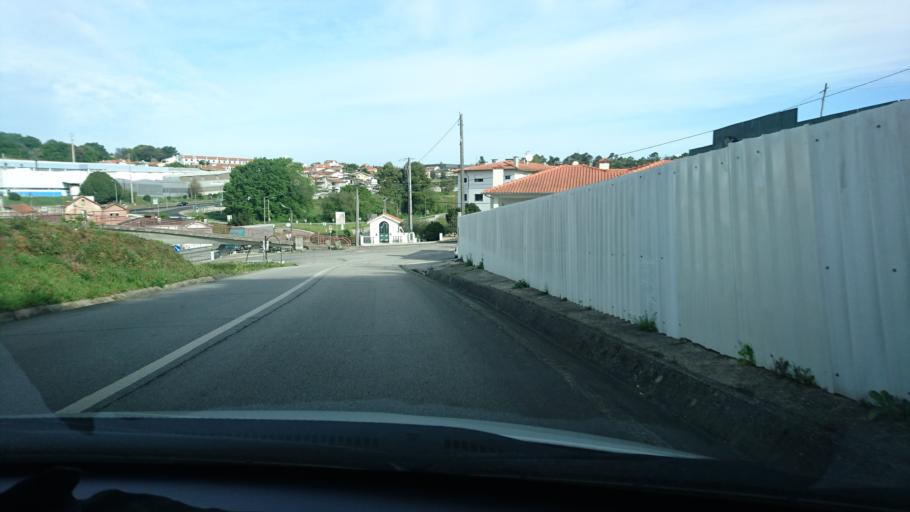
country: PT
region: Aveiro
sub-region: Oliveira de Azemeis
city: Sao Roque
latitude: 40.8745
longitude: -8.4858
